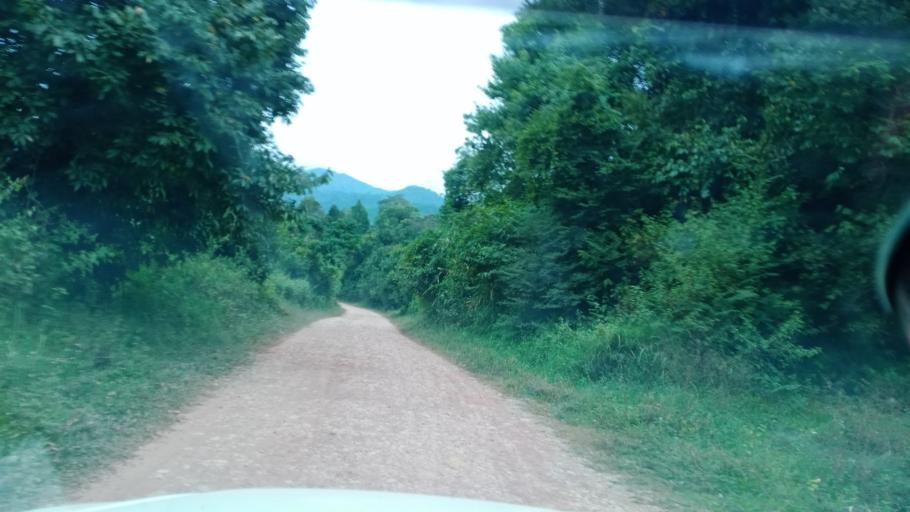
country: TH
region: Changwat Bueng Kan
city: Pak Khat
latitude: 18.7148
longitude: 103.2227
